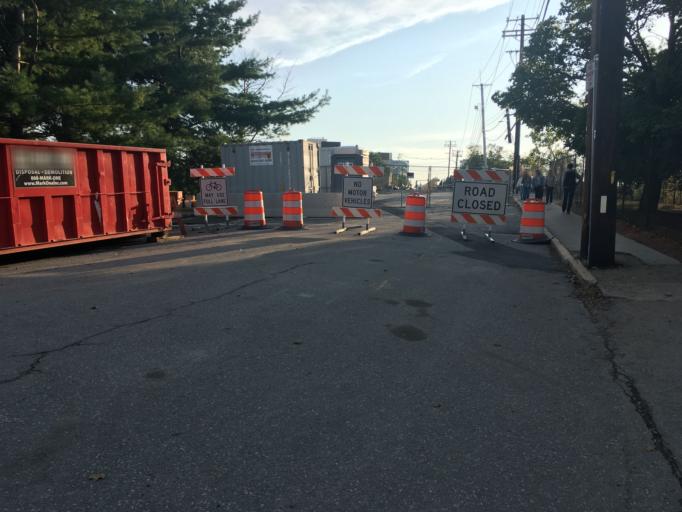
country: US
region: Massachusetts
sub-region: Middlesex County
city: Lowell
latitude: 42.6522
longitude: -71.3217
